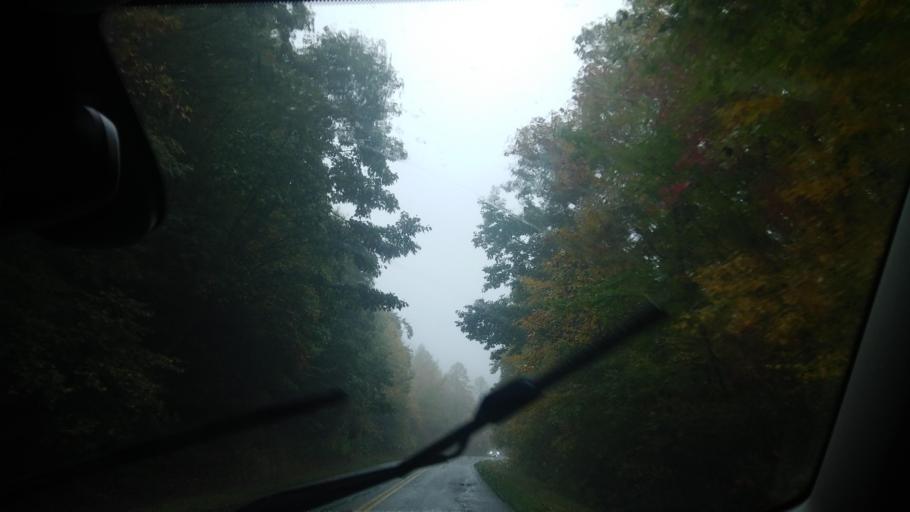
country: US
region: North Carolina
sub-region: Watauga County
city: Foscoe
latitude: 36.1217
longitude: -81.7757
